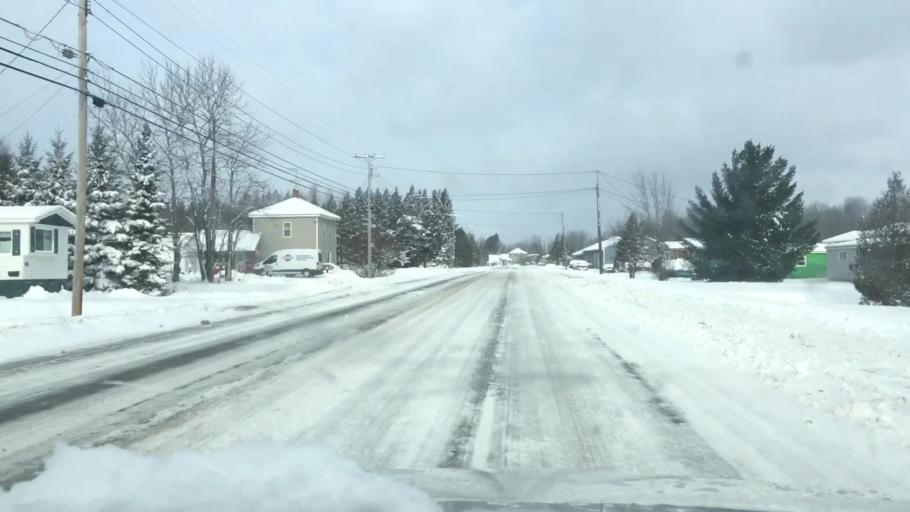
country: US
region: Maine
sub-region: Aroostook County
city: Van Buren
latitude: 47.1740
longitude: -67.9467
